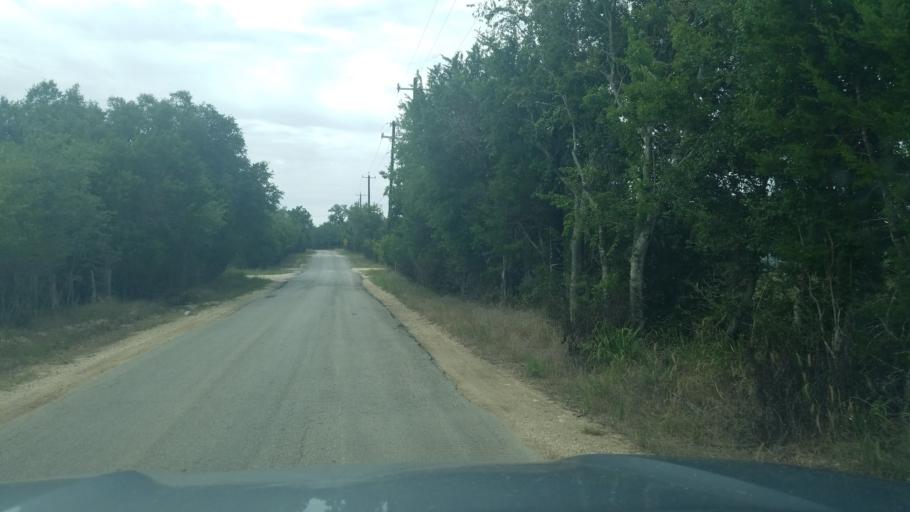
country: US
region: Texas
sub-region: Comal County
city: Bulverde
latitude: 29.7701
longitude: -98.4138
